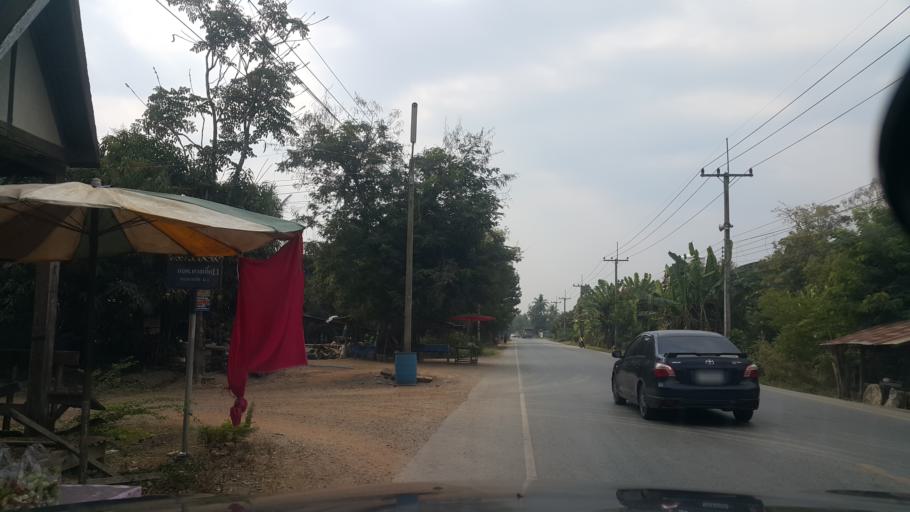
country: TH
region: Sukhothai
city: Si Samrong
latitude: 17.0841
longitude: 99.8818
